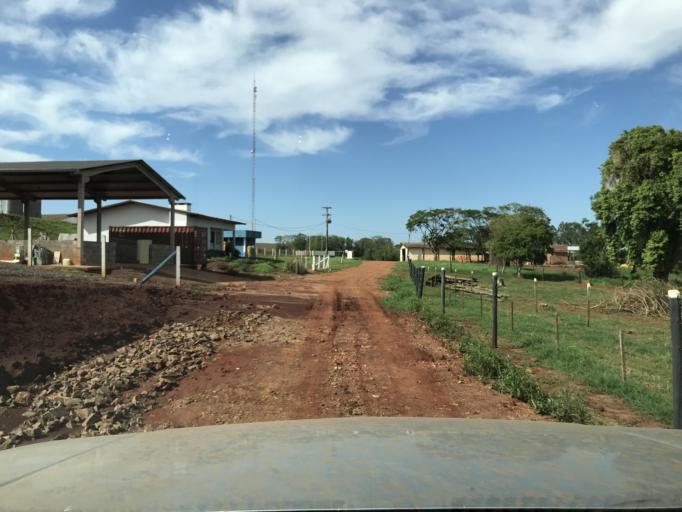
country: BR
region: Parana
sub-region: Palotina
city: Palotina
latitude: -24.1790
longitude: -53.8385
